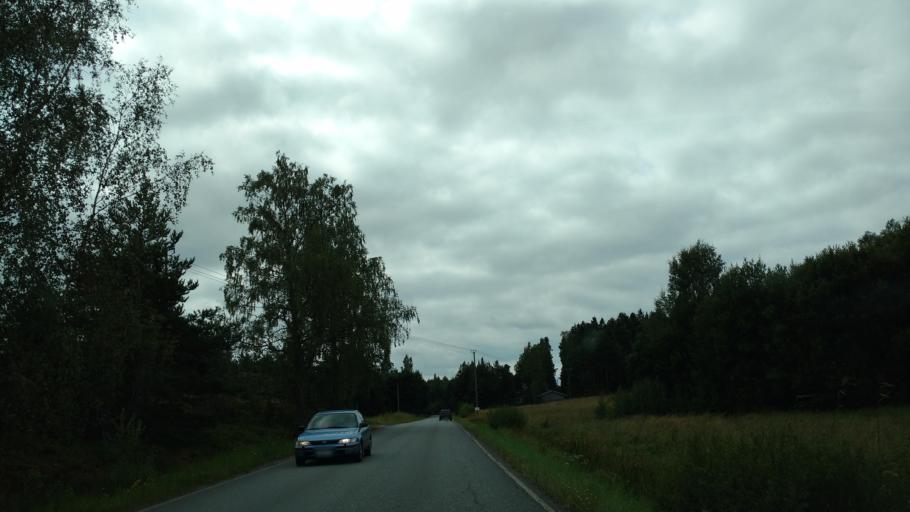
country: FI
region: Varsinais-Suomi
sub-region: Aboland-Turunmaa
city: Dragsfjaerd
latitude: 59.9698
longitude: 22.4459
